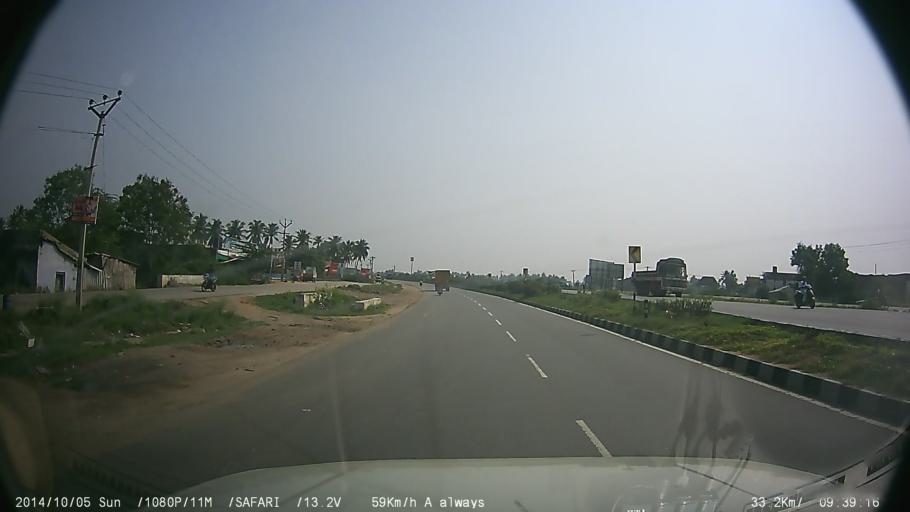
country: IN
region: Tamil Nadu
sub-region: Erode
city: Bhavani
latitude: 11.4375
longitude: 77.7080
